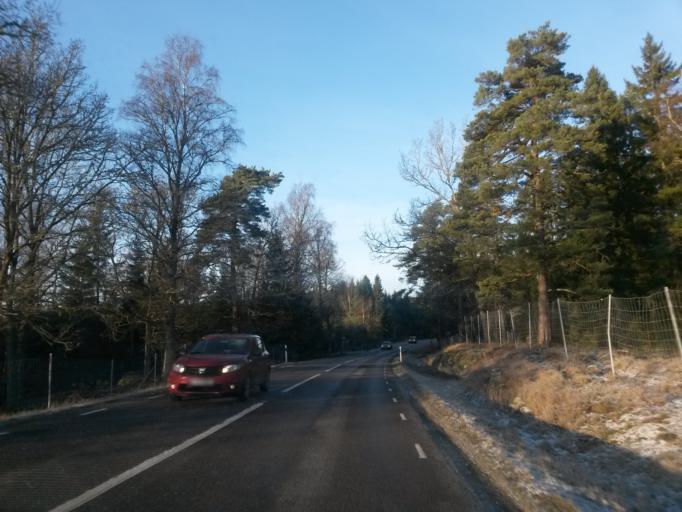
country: SE
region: Vaestra Goetaland
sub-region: Alingsas Kommun
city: Sollebrunn
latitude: 58.1400
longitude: 12.4224
